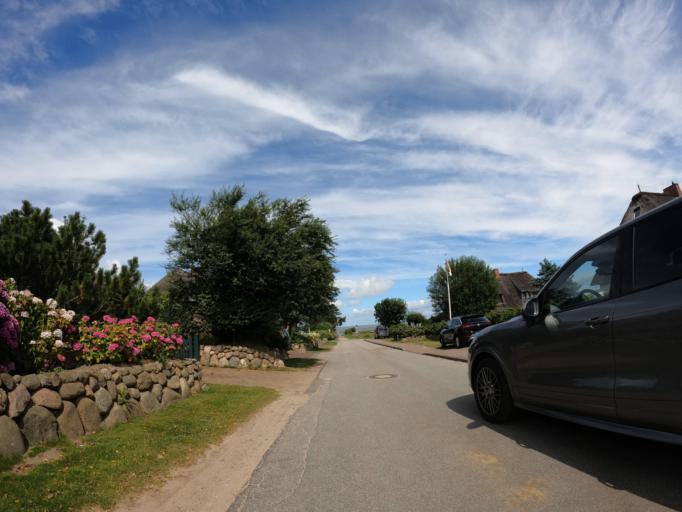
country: DE
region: Schleswig-Holstein
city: Sylt-Ost
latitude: 54.8750
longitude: 8.4437
